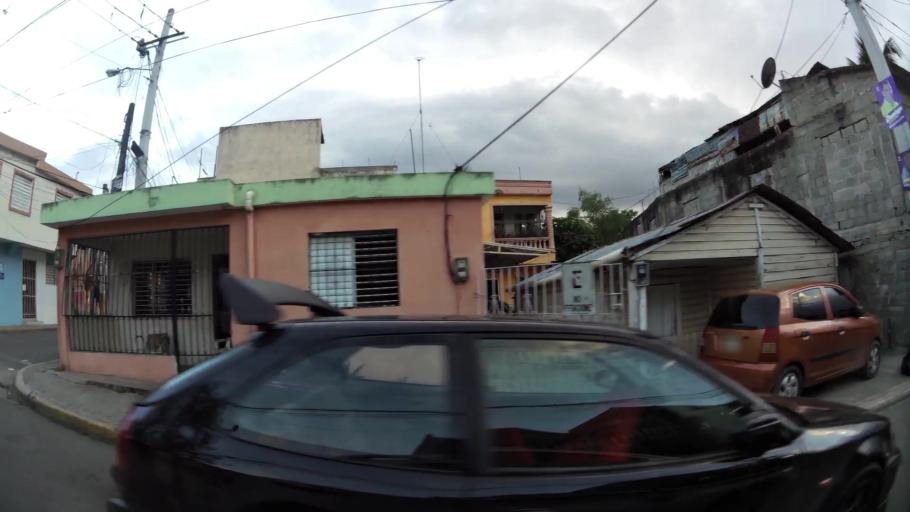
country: DO
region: Santo Domingo
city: Santo Domingo Oeste
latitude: 18.5251
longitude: -70.0161
